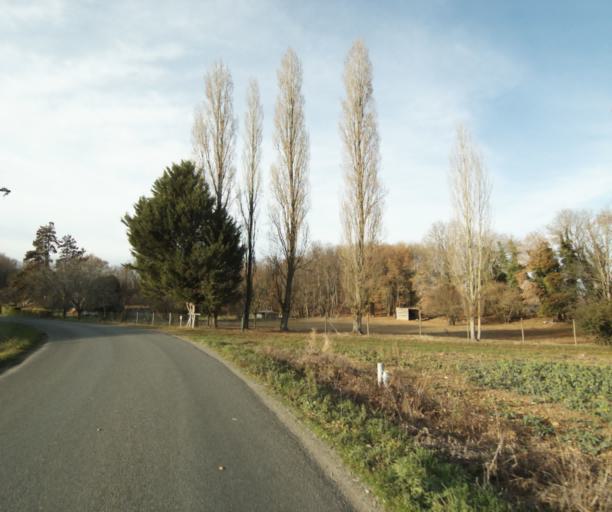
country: FR
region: Poitou-Charentes
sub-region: Departement de la Charente-Maritime
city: Saint-Hilaire-de-Villefranche
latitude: 45.8115
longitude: -0.5585
